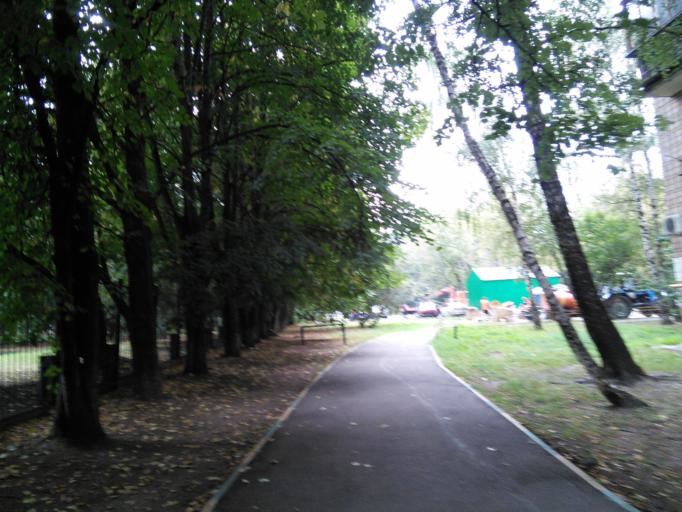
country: RU
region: Moscow
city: Tsaritsyno
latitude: 55.6355
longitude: 37.6685
